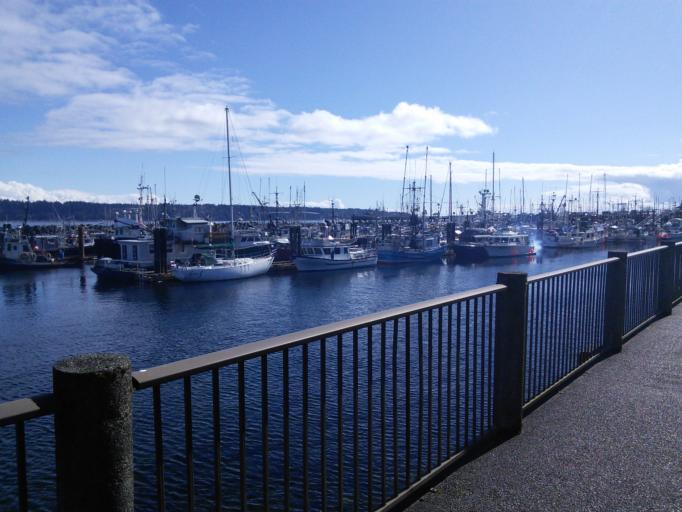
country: CA
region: British Columbia
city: Campbell River
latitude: 50.0241
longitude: -125.2400
